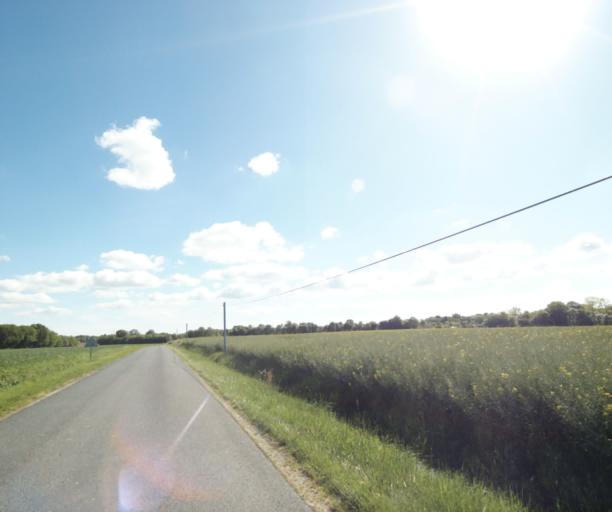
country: FR
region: Poitou-Charentes
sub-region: Departement de la Charente-Maritime
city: Saint-Georges-des-Coteaux
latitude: 45.7899
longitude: -0.6952
